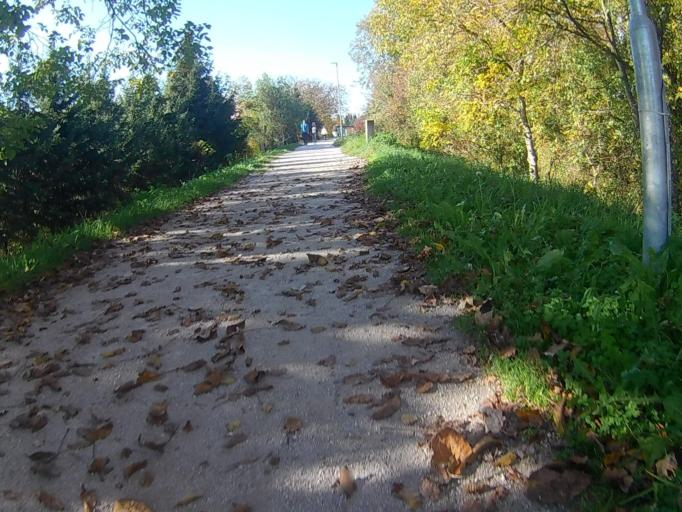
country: SI
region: Ptuj
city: Ptuj
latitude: 46.4207
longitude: 15.8602
